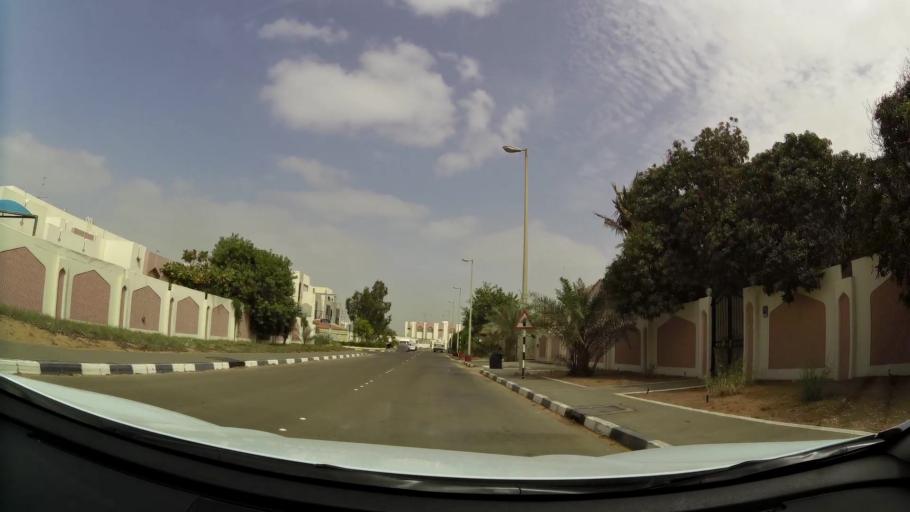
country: AE
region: Abu Dhabi
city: Abu Dhabi
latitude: 24.3933
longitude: 54.5075
